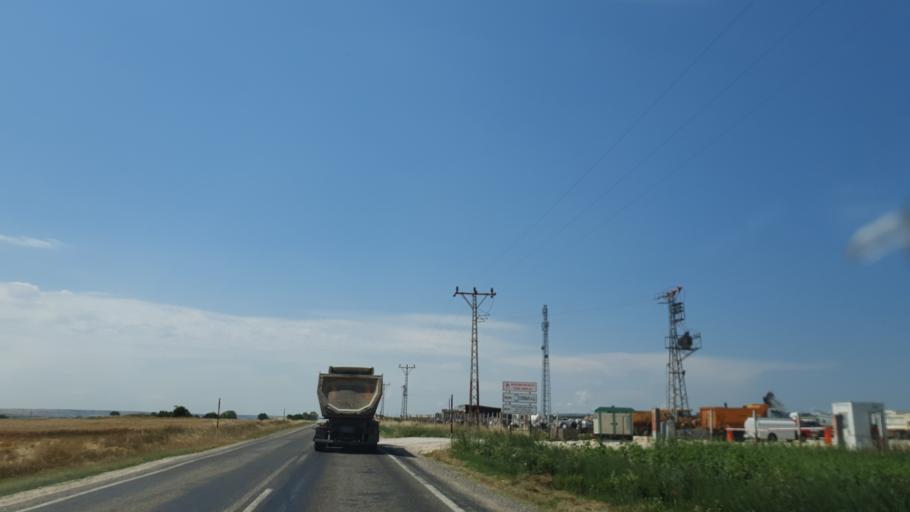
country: TR
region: Tekirdag
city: Saray
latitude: 41.5184
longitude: 27.8607
